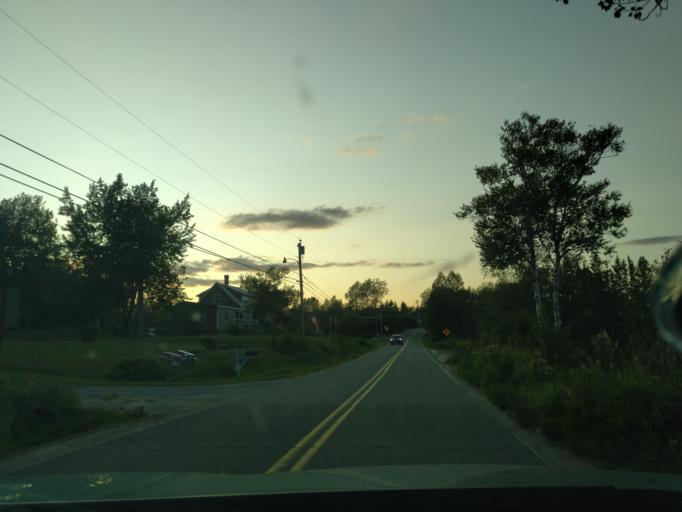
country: US
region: Maine
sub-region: Hancock County
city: Gouldsboro
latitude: 44.3852
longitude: -68.0379
